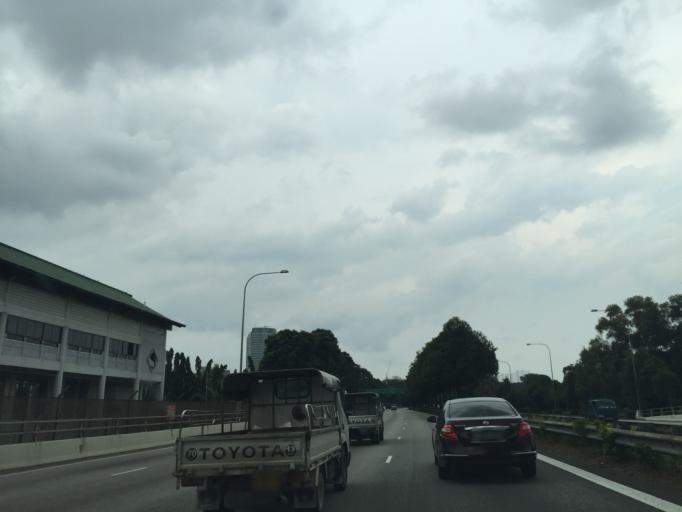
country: SG
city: Singapore
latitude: 1.3267
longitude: 103.7329
